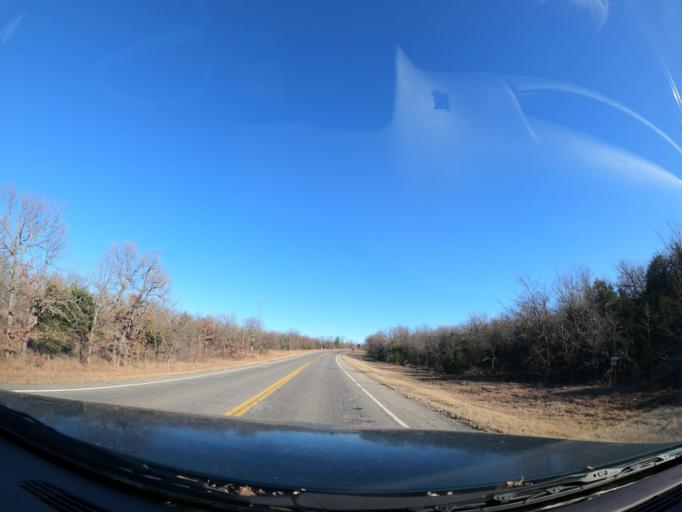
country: US
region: Oklahoma
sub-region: Pittsburg County
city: Longtown
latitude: 35.2251
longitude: -95.4359
